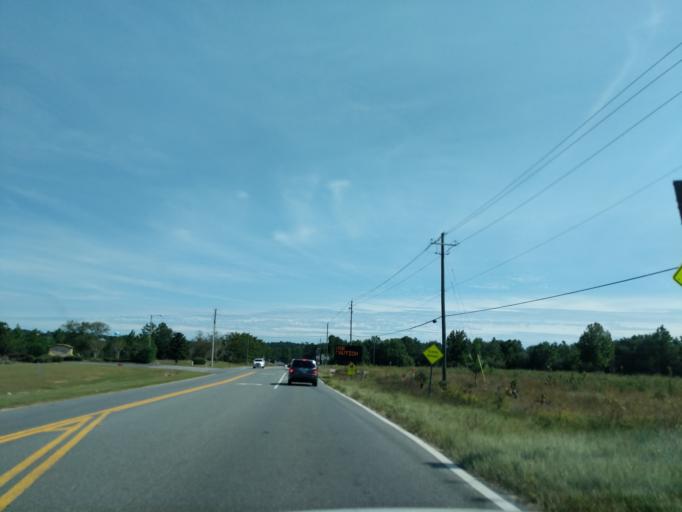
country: US
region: Florida
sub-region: Okaloosa County
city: Crestview
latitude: 30.7149
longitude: -86.6083
